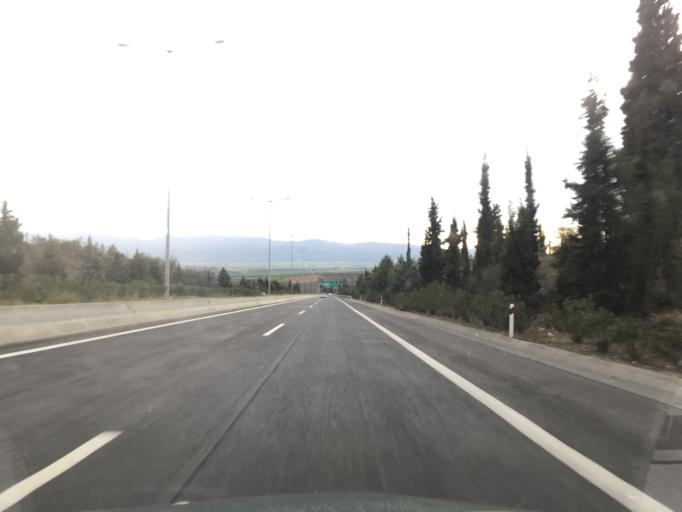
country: GR
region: Thessaly
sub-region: Nomos Magnisias
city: Nea Anchialos
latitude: 39.2767
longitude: 22.7429
